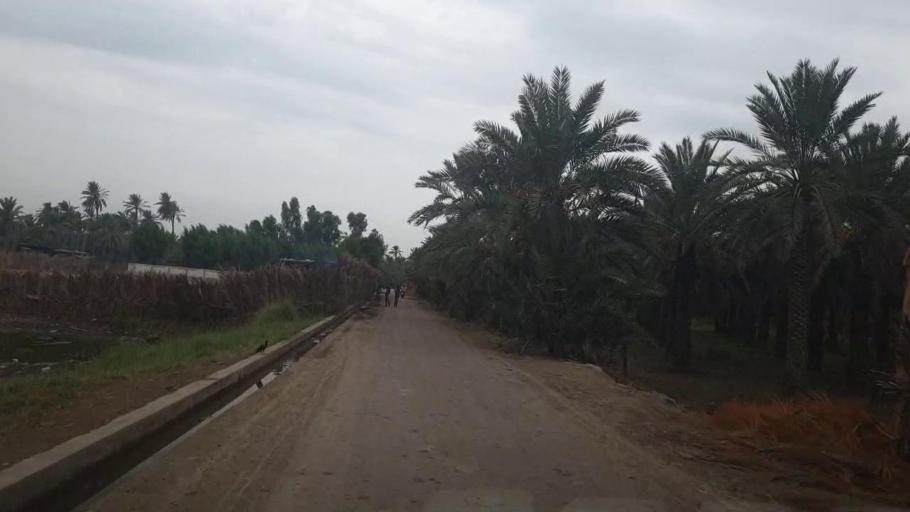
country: PK
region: Sindh
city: Khairpur
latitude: 27.5766
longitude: 68.7456
